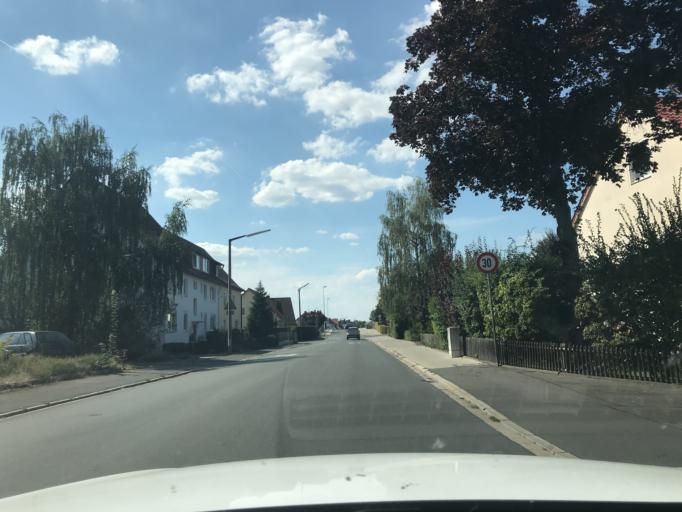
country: DE
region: Bavaria
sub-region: Regierungsbezirk Mittelfranken
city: Erlangen
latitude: 49.5665
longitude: 10.9988
